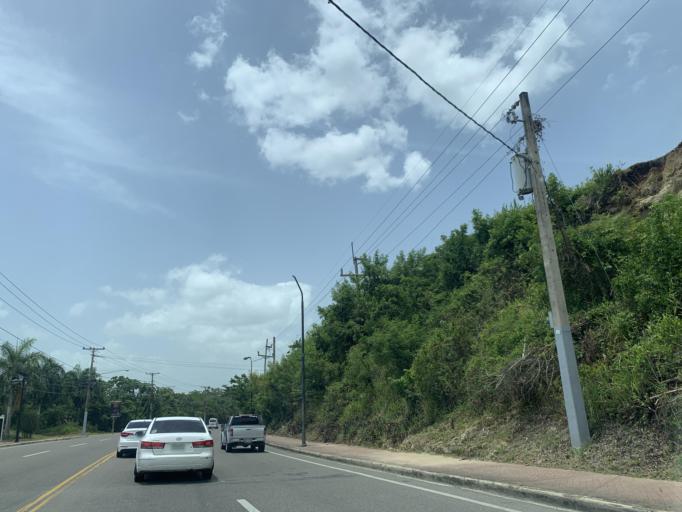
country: DO
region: Puerto Plata
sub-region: Puerto Plata
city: Puerto Plata
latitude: 19.7728
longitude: -70.6556
